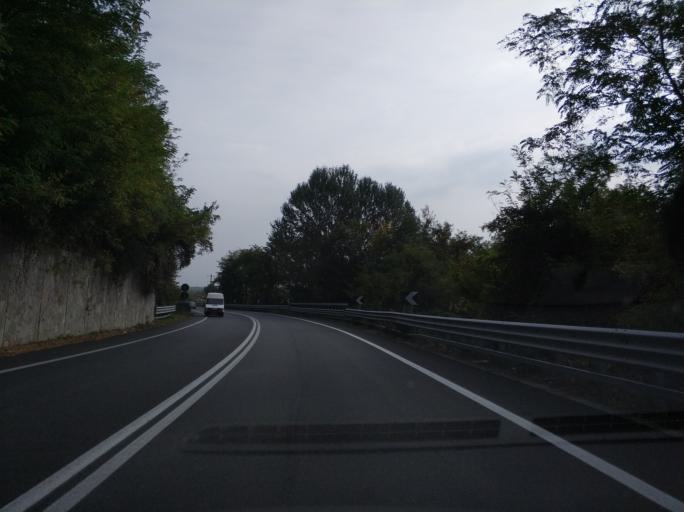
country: IT
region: Piedmont
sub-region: Provincia di Torino
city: Parella
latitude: 45.4230
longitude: 7.7912
